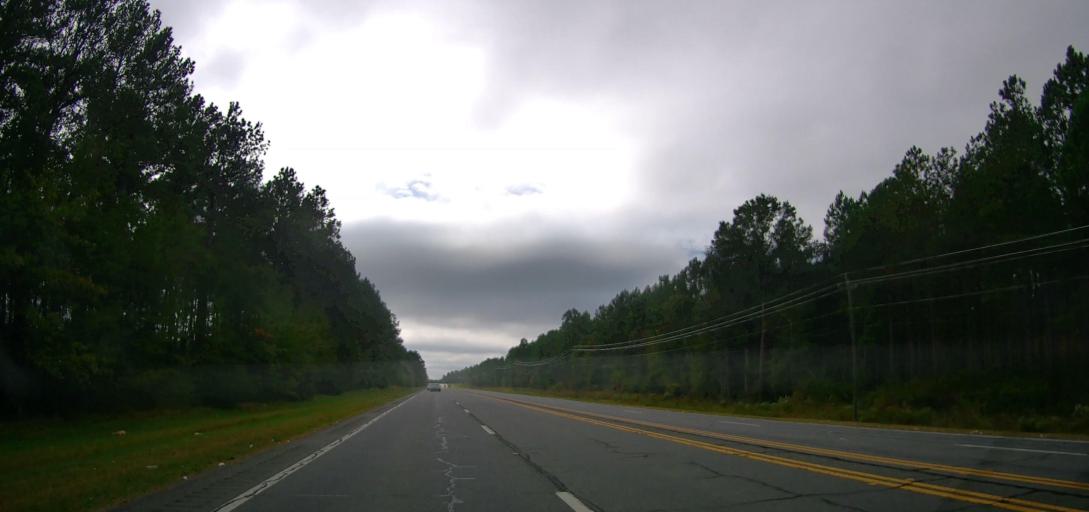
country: US
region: Georgia
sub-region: Colquitt County
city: Moultrie
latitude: 31.2358
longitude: -83.7371
